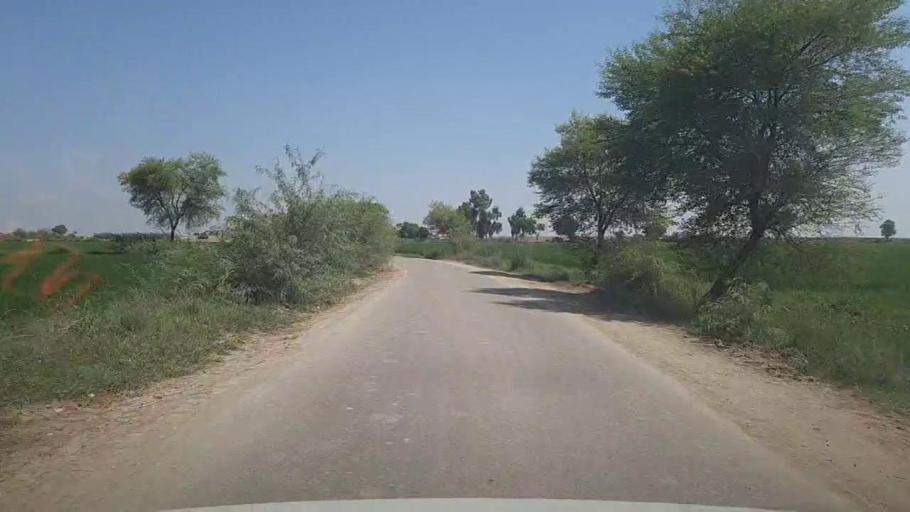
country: PK
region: Sindh
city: Kashmor
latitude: 28.2827
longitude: 69.4395
